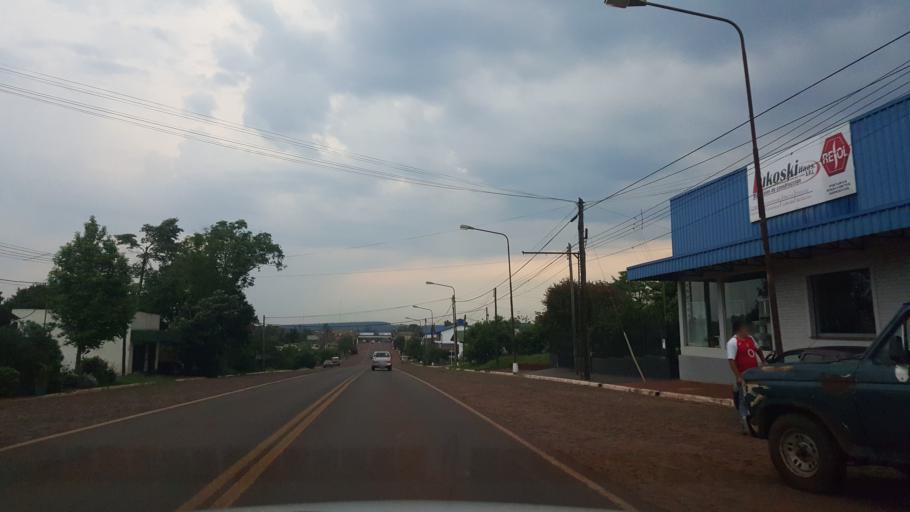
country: AR
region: Misiones
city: Gobernador Roca
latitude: -27.1881
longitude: -55.4664
